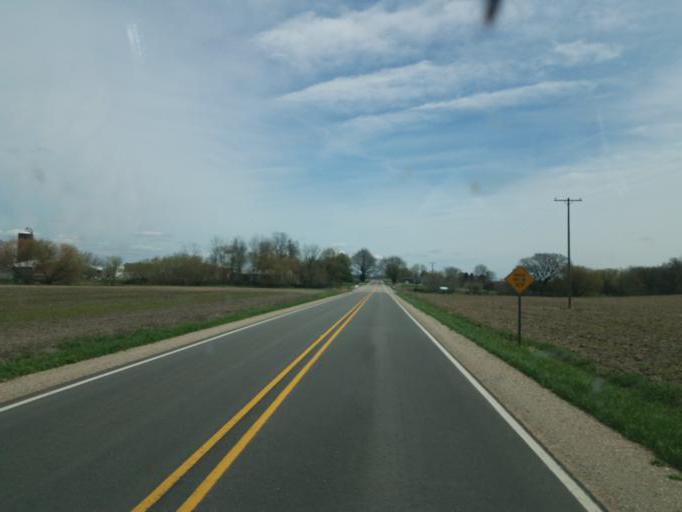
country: US
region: Michigan
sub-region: Isabella County
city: Lake Isabella
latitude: 43.6269
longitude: -84.8862
